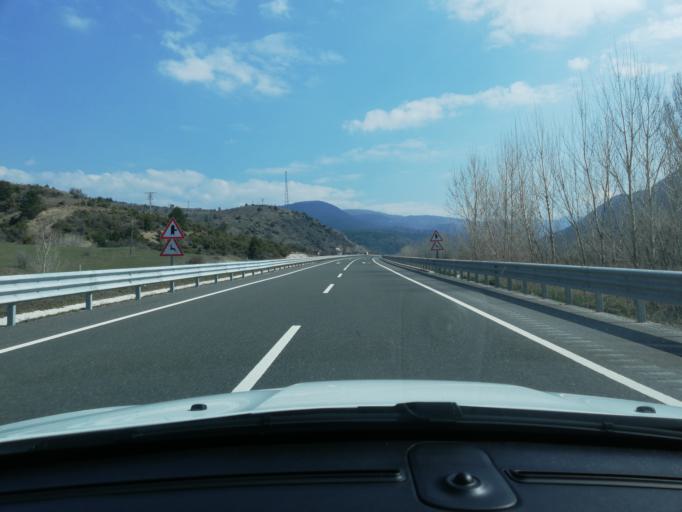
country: TR
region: Cankiri
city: Ilgaz
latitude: 40.9680
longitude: 33.6863
